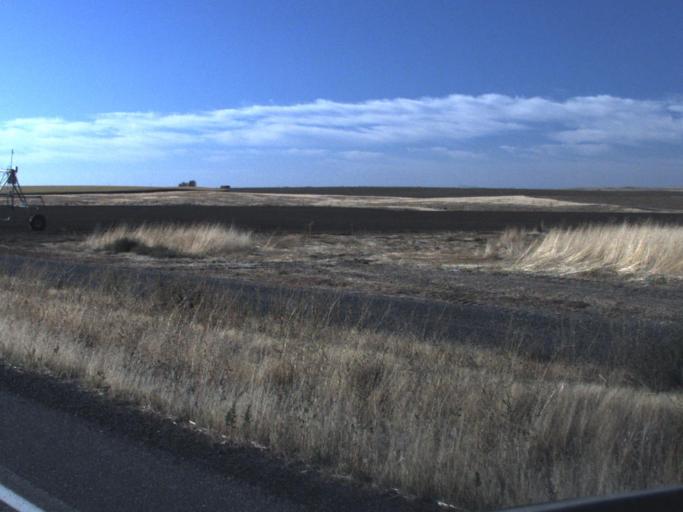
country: US
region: Washington
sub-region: Walla Walla County
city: Garrett
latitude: 46.2966
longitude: -118.6472
